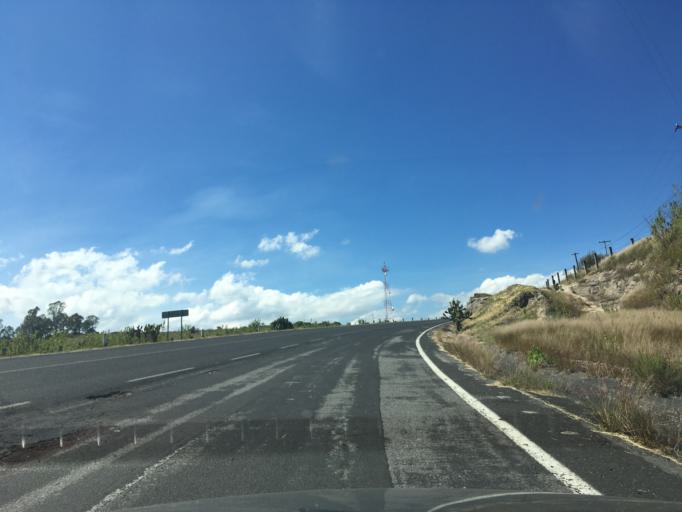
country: MX
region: Mexico
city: Huaniqueo de Morales
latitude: 19.8812
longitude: -101.5117
